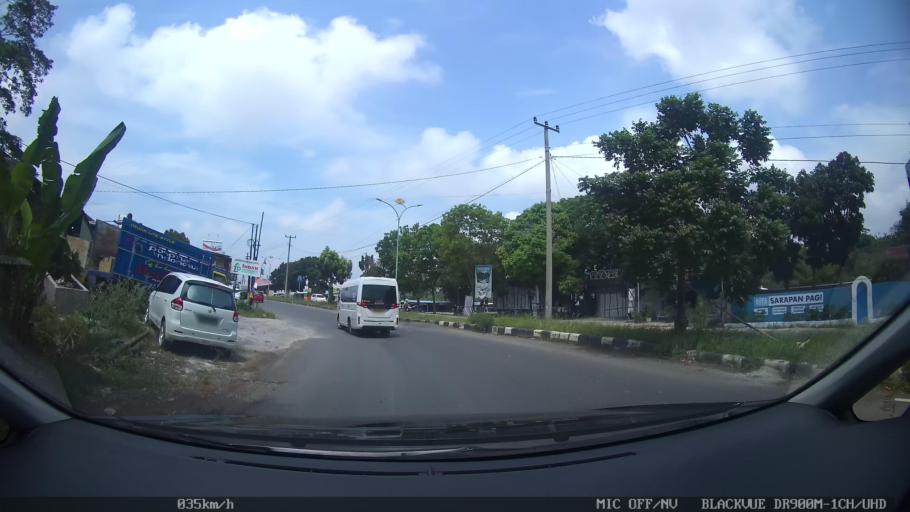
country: ID
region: Lampung
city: Kedaton
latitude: -5.3587
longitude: 105.3060
